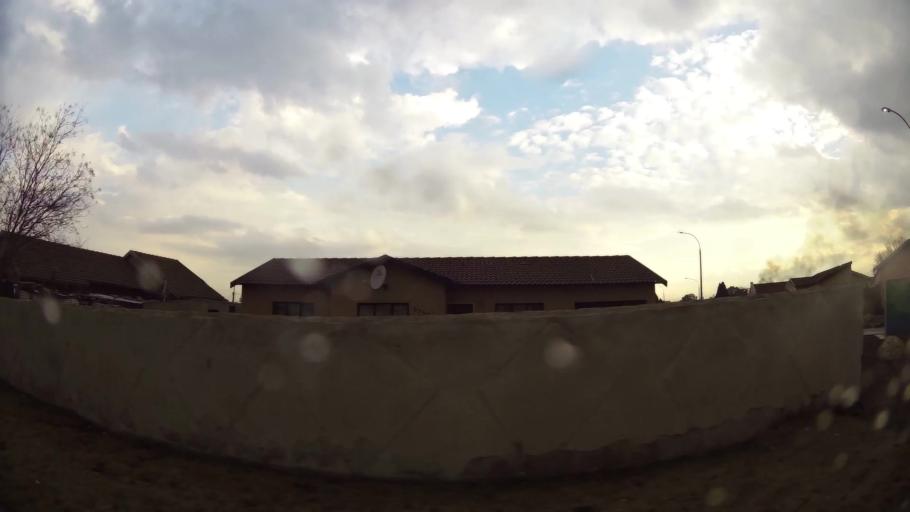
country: ZA
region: Gauteng
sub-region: Ekurhuleni Metropolitan Municipality
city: Germiston
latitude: -26.3543
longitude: 28.1286
